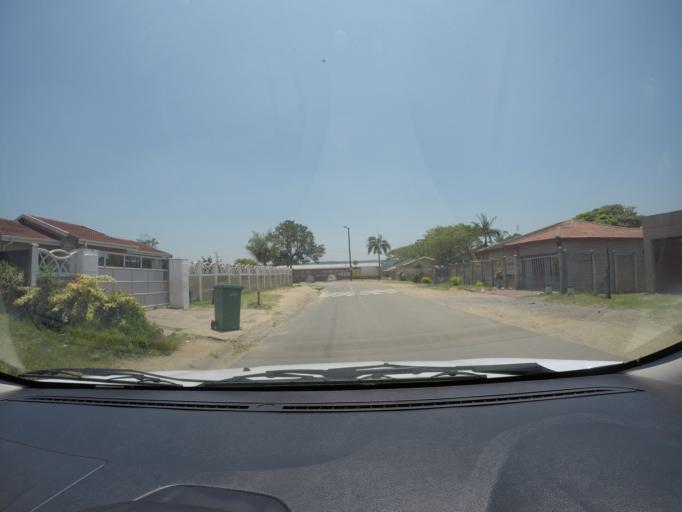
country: ZA
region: KwaZulu-Natal
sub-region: uThungulu District Municipality
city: eSikhawini
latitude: -28.8841
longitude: 31.8981
